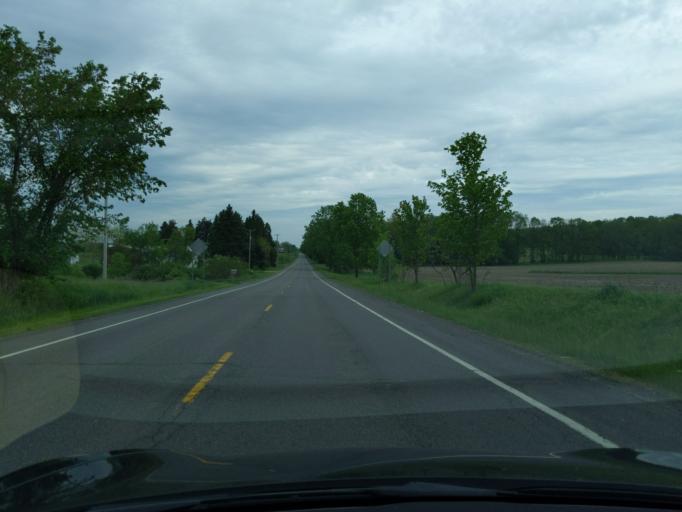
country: US
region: Michigan
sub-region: Ingham County
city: Mason
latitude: 42.5572
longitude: -84.3568
